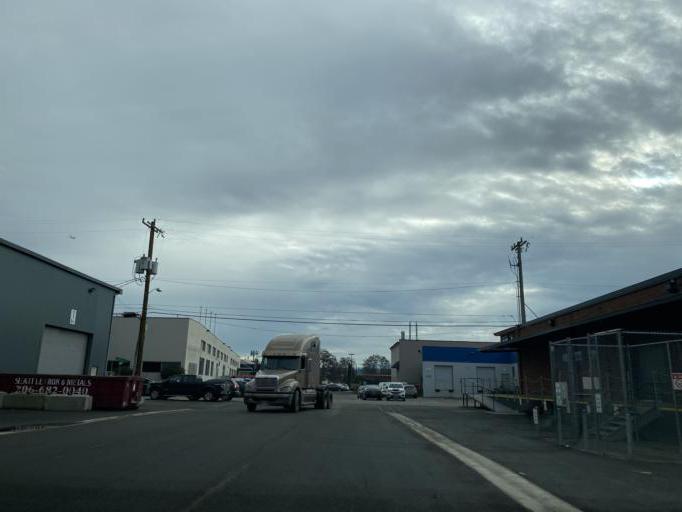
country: US
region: Washington
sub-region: King County
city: White Center
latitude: 47.5579
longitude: -122.3325
